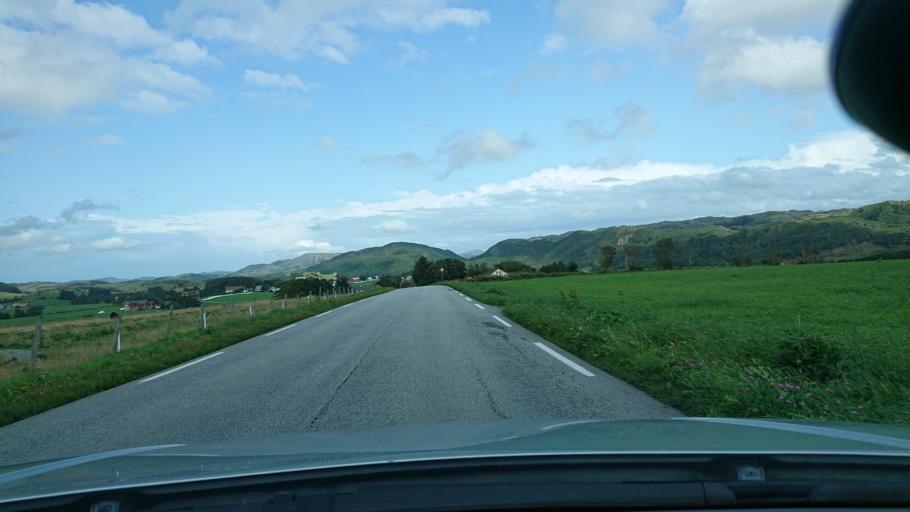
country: NO
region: Rogaland
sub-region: Gjesdal
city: Algard
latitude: 58.6935
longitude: 5.7743
